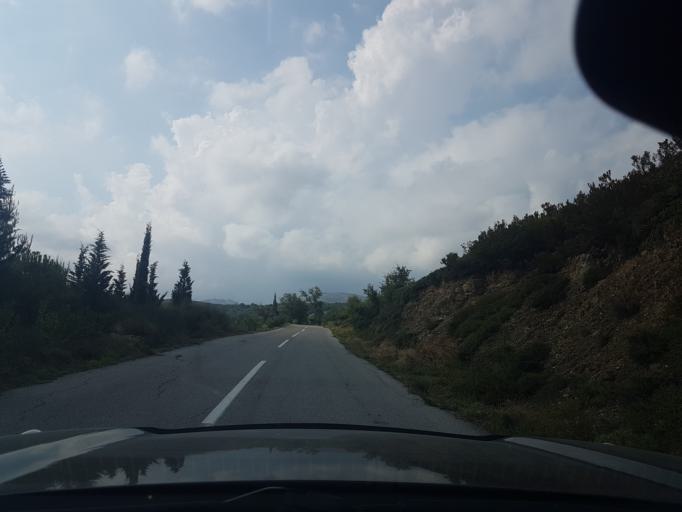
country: GR
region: Central Greece
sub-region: Nomos Evvoias
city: Yimnon
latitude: 38.5374
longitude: 23.9700
